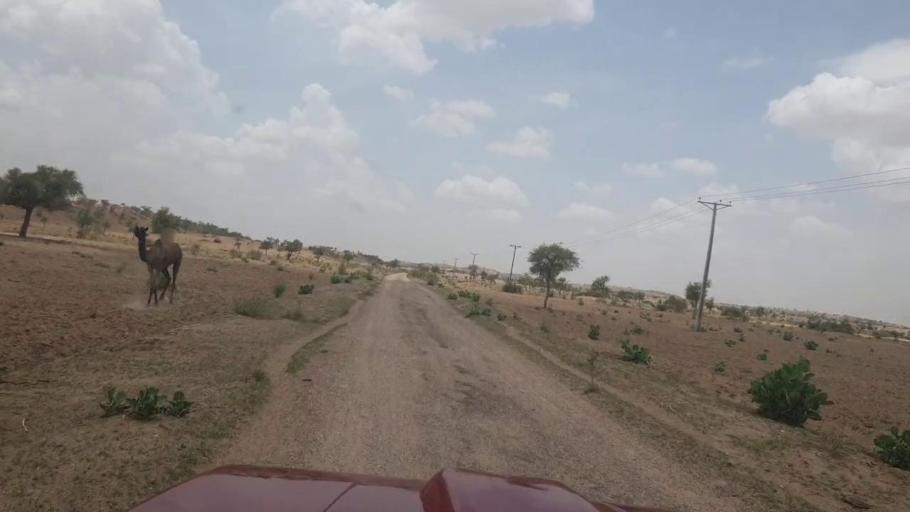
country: PK
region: Sindh
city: Islamkot
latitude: 25.2055
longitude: 70.4468
